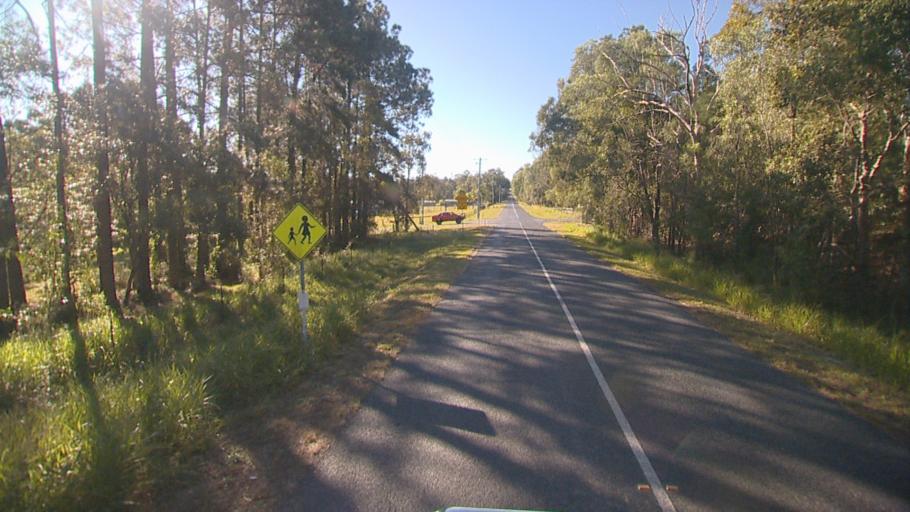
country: AU
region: Queensland
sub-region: Logan
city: Logan Reserve
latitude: -27.7362
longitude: 153.1035
